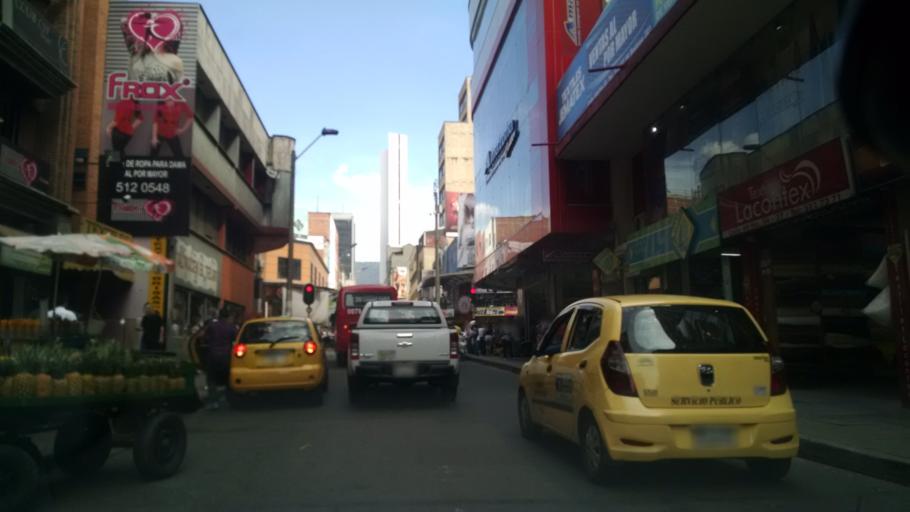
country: CO
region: Antioquia
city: Medellin
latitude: 6.2502
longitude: -75.5723
